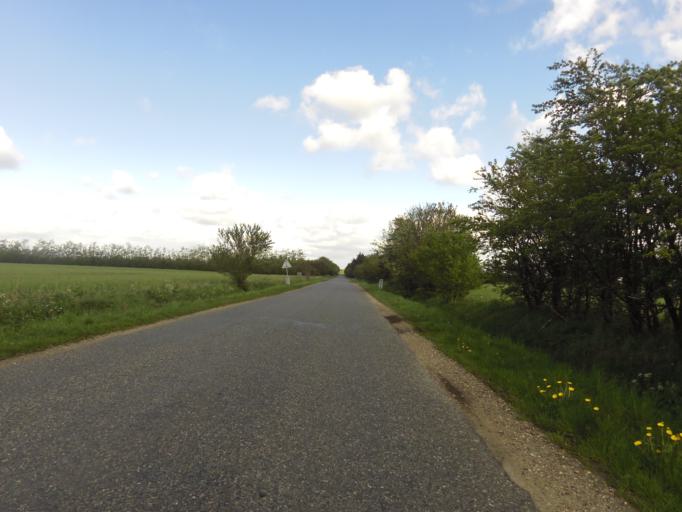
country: DK
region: South Denmark
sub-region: Esbjerg Kommune
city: Ribe
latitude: 55.2627
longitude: 8.7263
